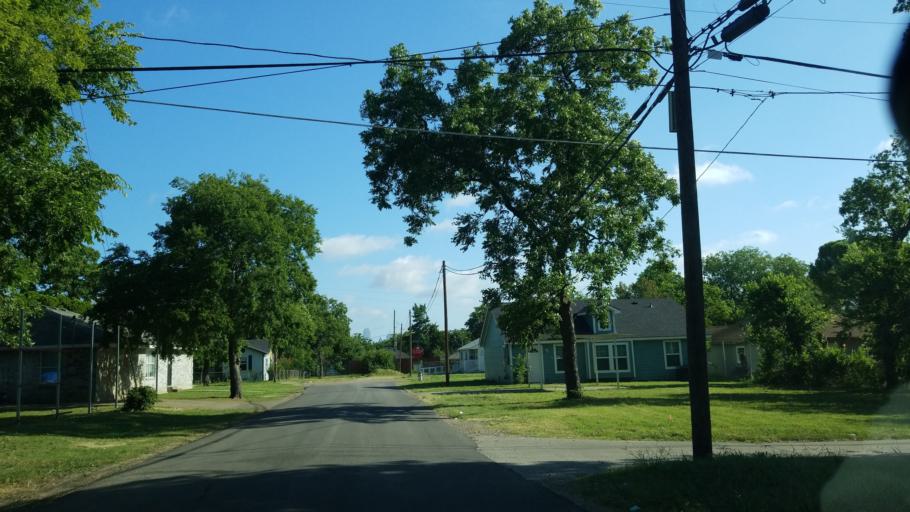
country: US
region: Texas
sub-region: Dallas County
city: Dallas
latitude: 32.7261
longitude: -96.8035
